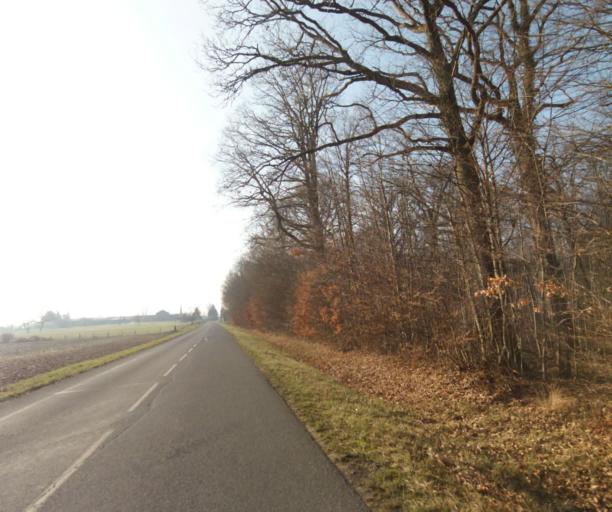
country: FR
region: Champagne-Ardenne
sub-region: Departement de la Haute-Marne
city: Laneuville-a-Remy
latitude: 48.4669
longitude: 4.9148
